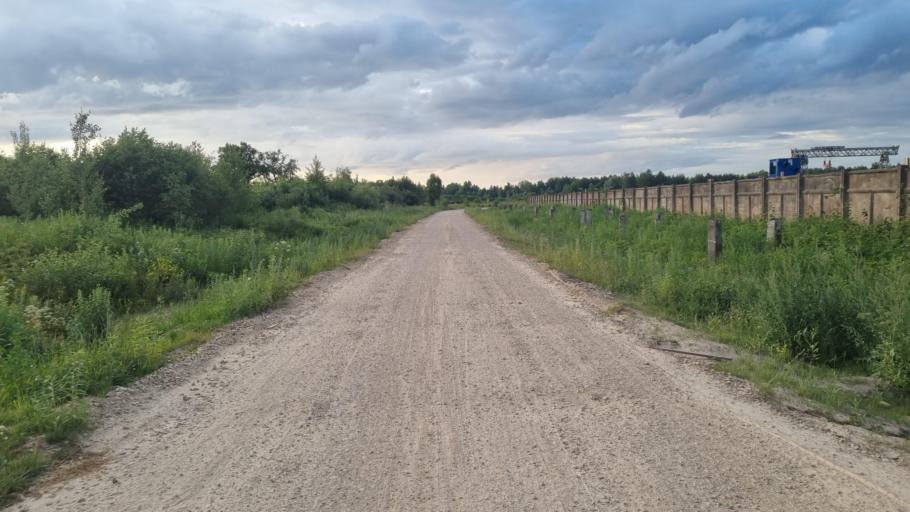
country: LV
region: Stopini
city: Ulbroka
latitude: 56.9142
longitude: 24.2391
